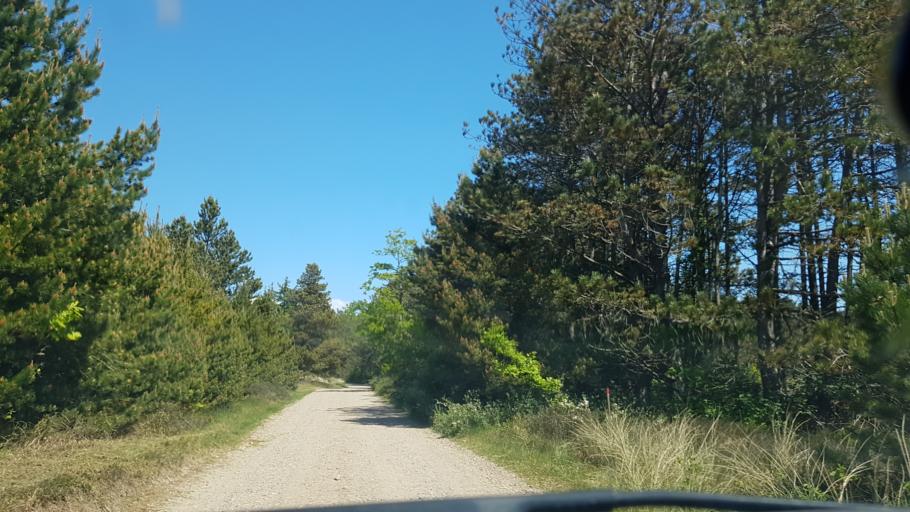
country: DE
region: Schleswig-Holstein
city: List
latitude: 55.1092
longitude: 8.5488
